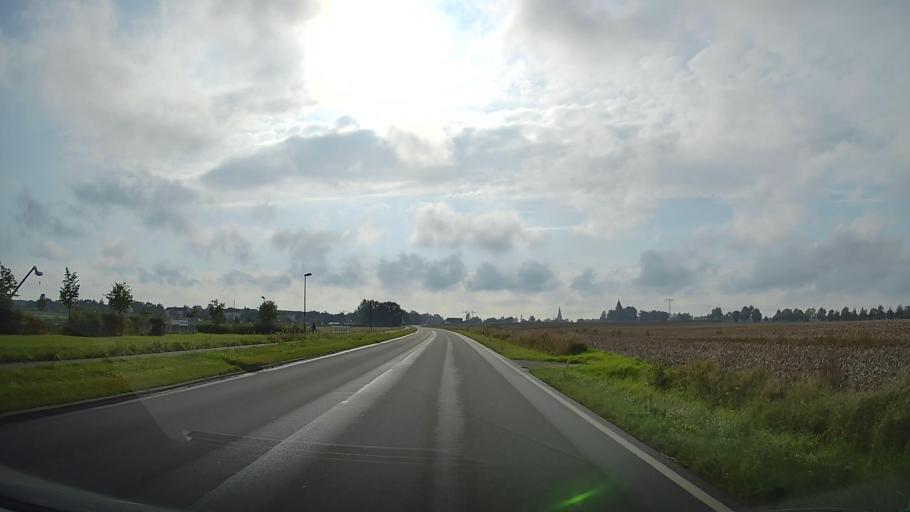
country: DE
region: Mecklenburg-Vorpommern
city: Hagenow
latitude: 53.4411
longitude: 11.2081
